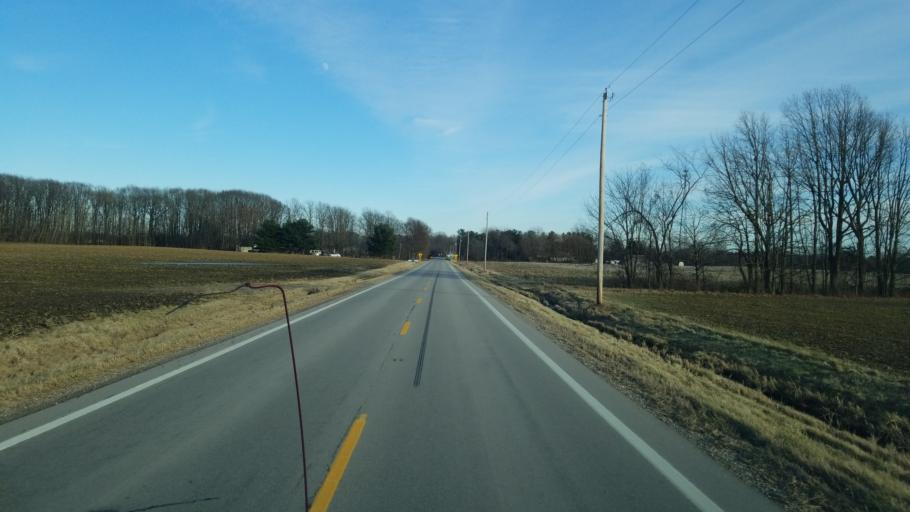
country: US
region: Ohio
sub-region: Huron County
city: Greenwich
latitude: 41.1025
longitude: -82.5021
